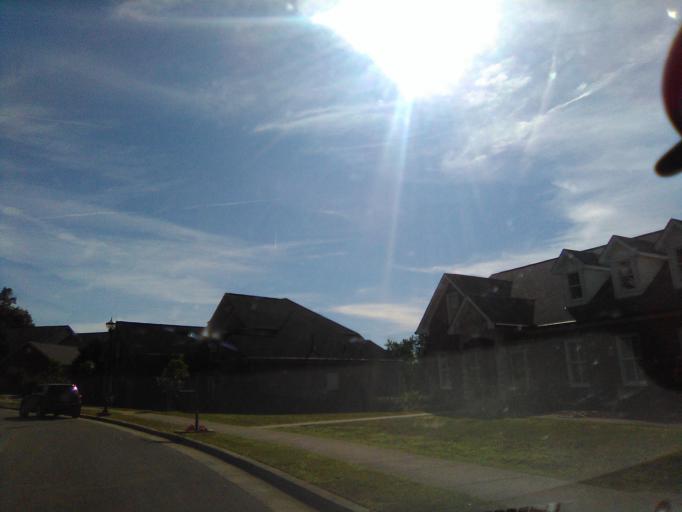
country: US
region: Tennessee
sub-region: Davidson County
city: Belle Meade
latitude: 36.1143
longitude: -86.9121
